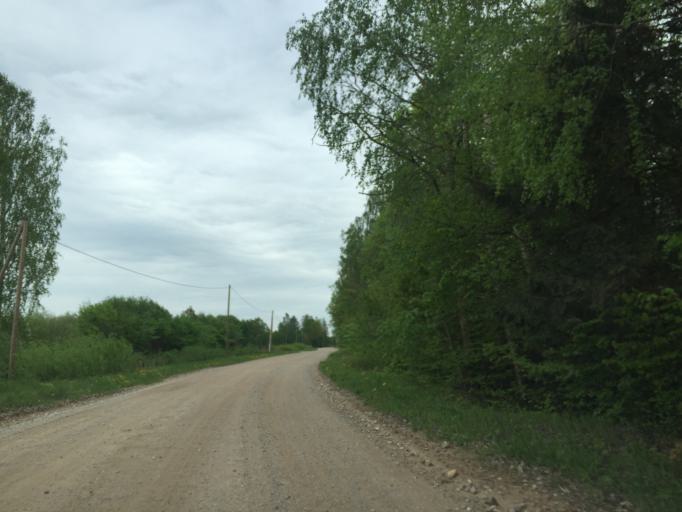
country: LV
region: Lielvarde
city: Lielvarde
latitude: 56.8057
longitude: 24.8566
